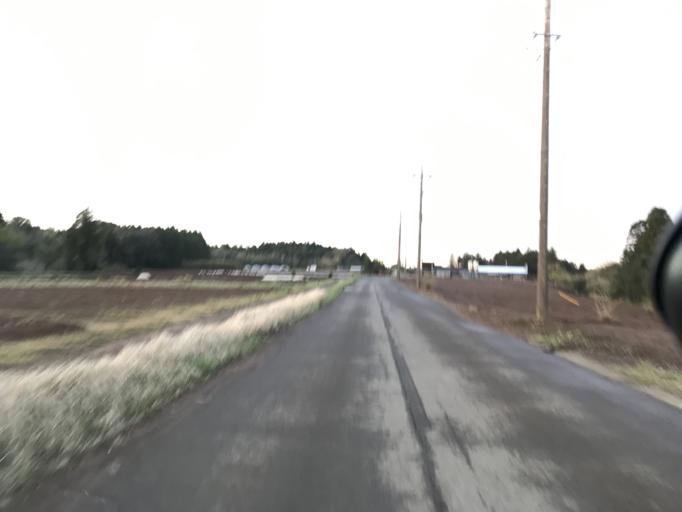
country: JP
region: Chiba
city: Sawara
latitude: 35.8243
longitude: 140.4963
